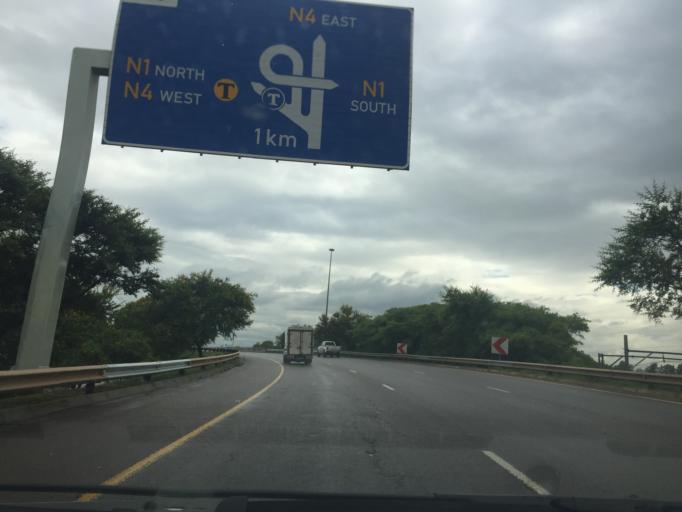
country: ZA
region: Gauteng
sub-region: City of Tshwane Metropolitan Municipality
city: Pretoria
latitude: -25.7440
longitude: 28.2480
